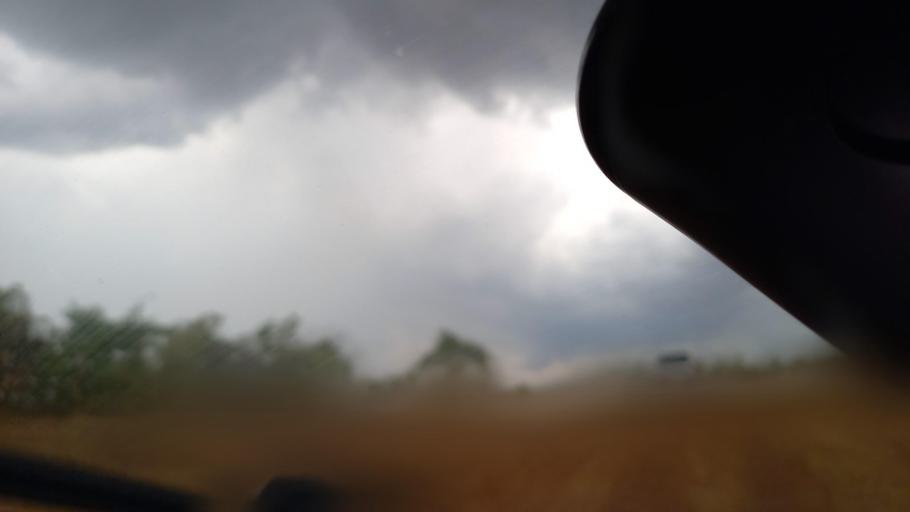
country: ZM
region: Lusaka
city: Kafue
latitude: -15.8669
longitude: 28.1880
